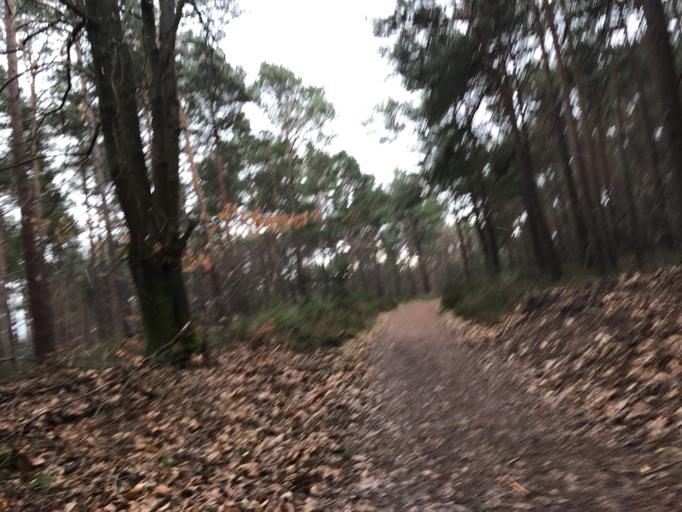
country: DE
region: Rheinland-Pfalz
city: Deidesheim
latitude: 49.4207
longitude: 8.1591
